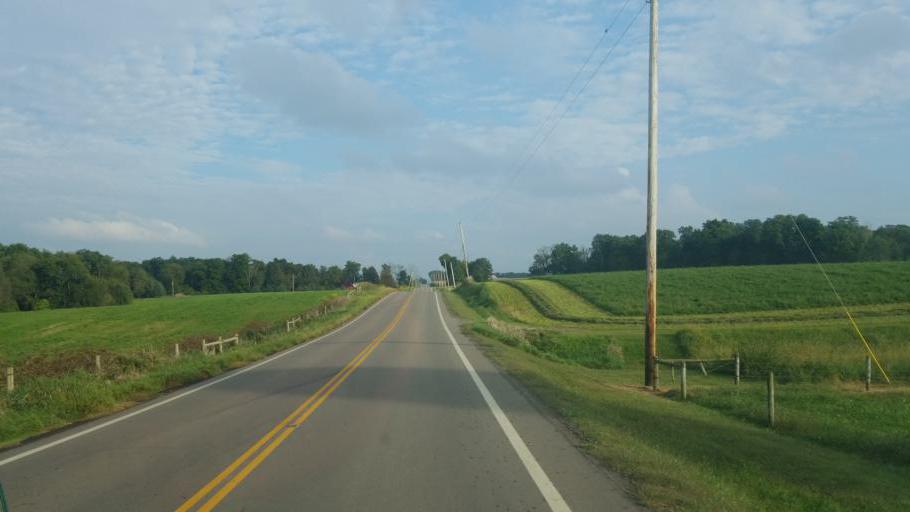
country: US
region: Ohio
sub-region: Wayne County
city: Wooster
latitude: 40.8538
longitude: -82.0375
